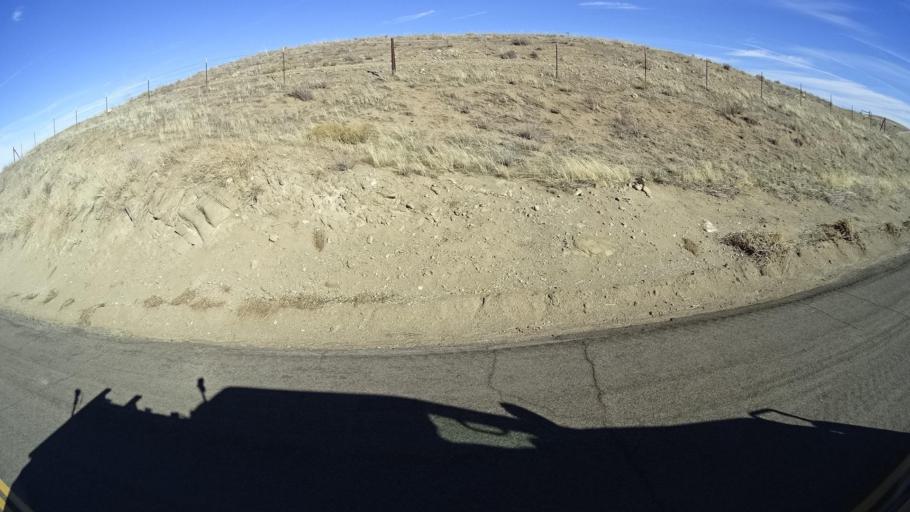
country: US
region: California
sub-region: Kern County
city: Maricopa
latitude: 34.9162
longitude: -119.4113
